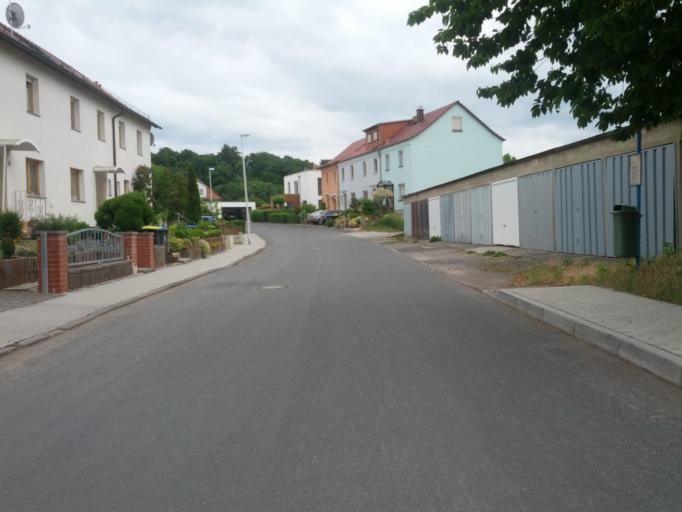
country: DE
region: Thuringia
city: Eisenach
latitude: 50.9860
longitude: 10.3258
